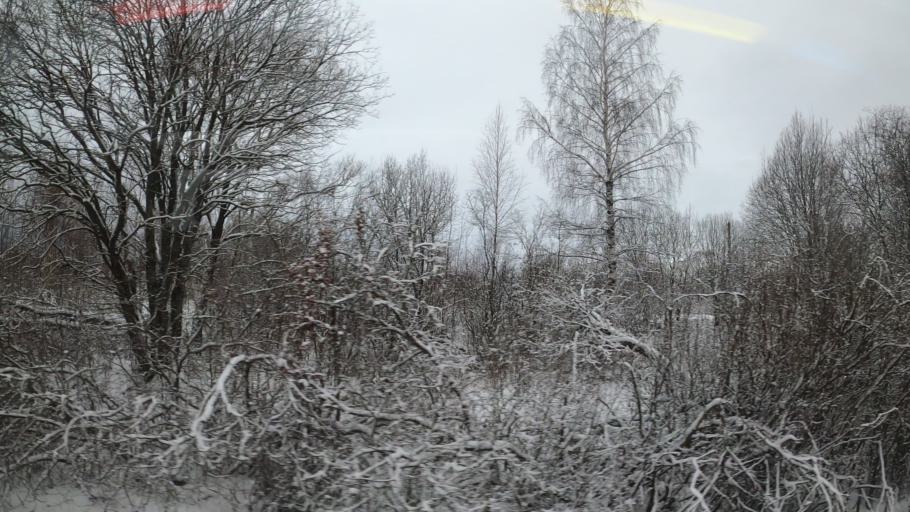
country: RU
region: Jaroslavl
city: Pereslavl'-Zalesskiy
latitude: 56.7300
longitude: 38.9016
